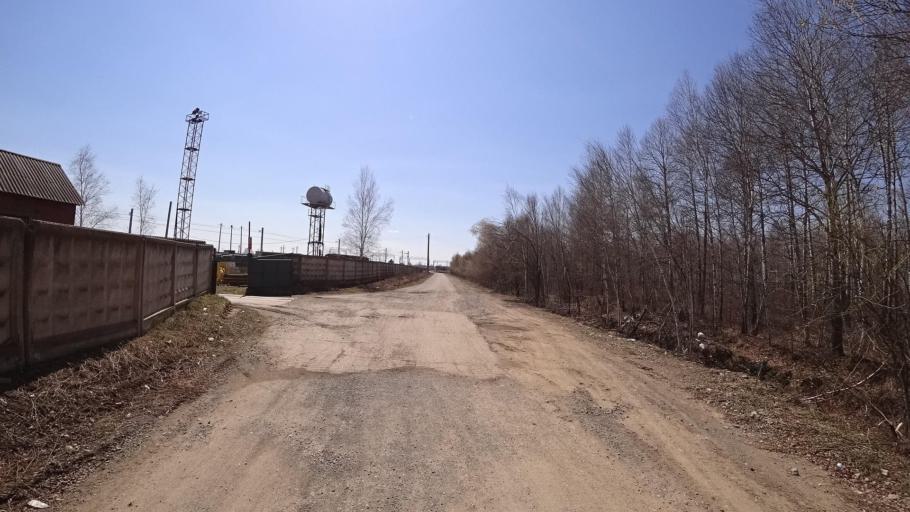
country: RU
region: Khabarovsk Krai
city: Khurba
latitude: 50.4144
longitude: 136.8821
